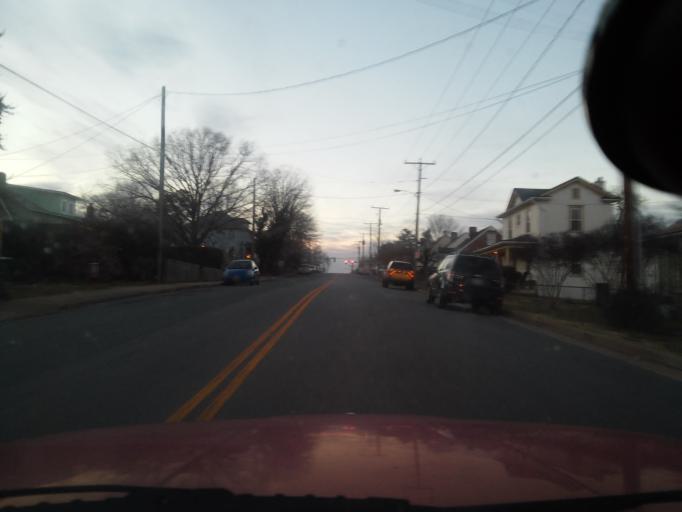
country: US
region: Virginia
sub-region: City of Charlottesville
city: Charlottesville
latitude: 38.0203
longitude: -78.4792
